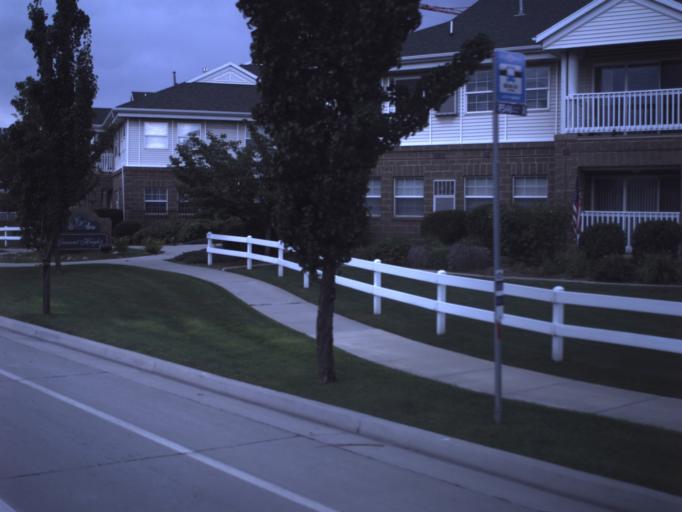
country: US
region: Utah
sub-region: Salt Lake County
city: White City
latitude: 40.5508
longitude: -111.8724
